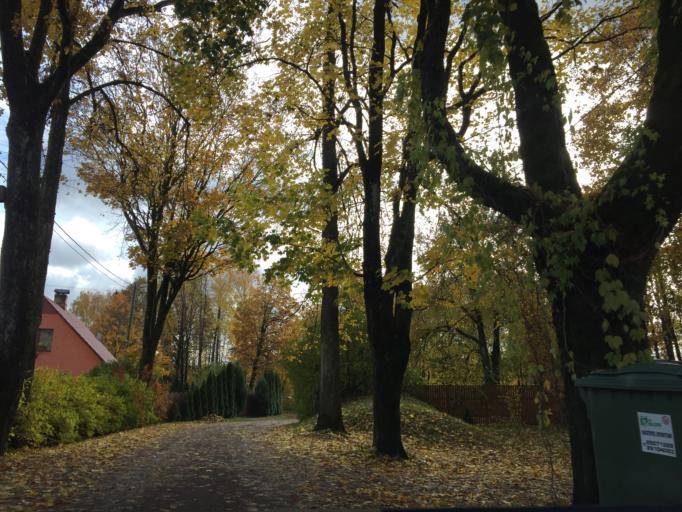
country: LV
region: Lielvarde
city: Lielvarde
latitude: 56.7172
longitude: 24.8327
